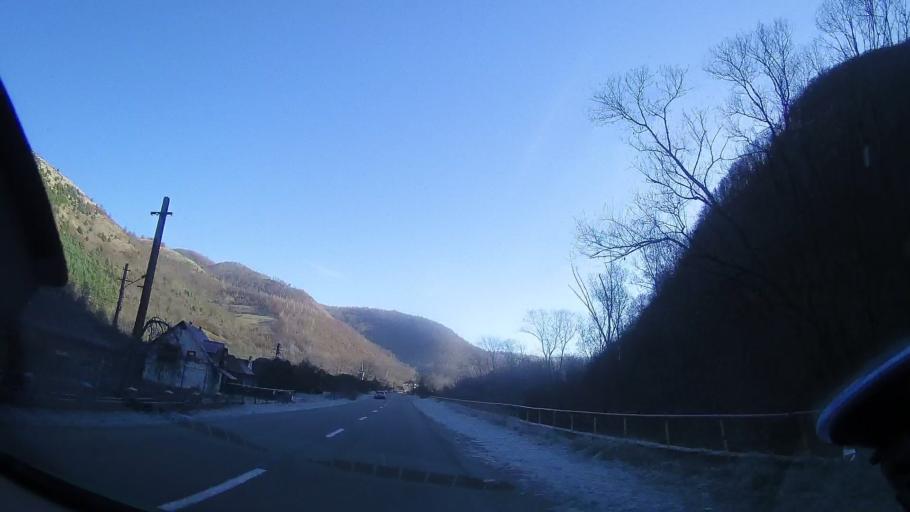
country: RO
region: Bihor
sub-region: Comuna Bulz
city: Bulz
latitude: 46.9143
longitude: 22.6690
